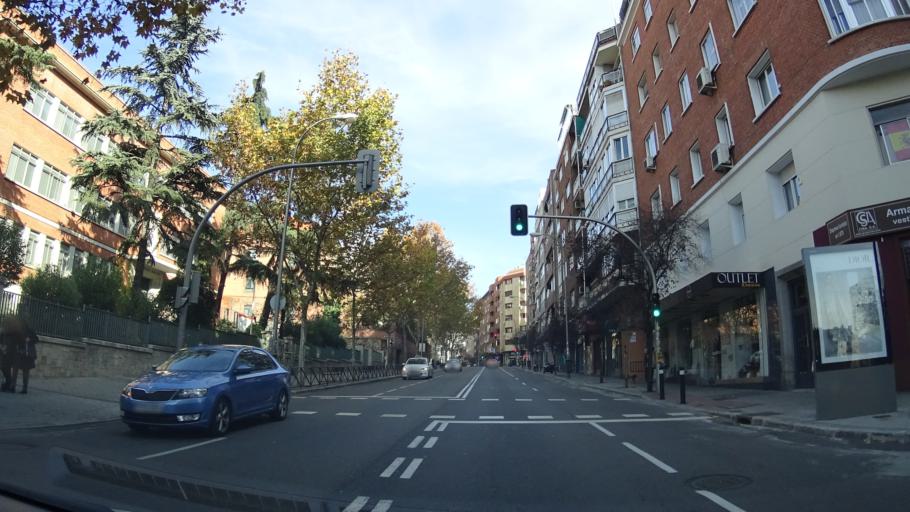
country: ES
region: Madrid
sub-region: Provincia de Madrid
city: Salamanca
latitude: 40.4420
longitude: -3.6771
